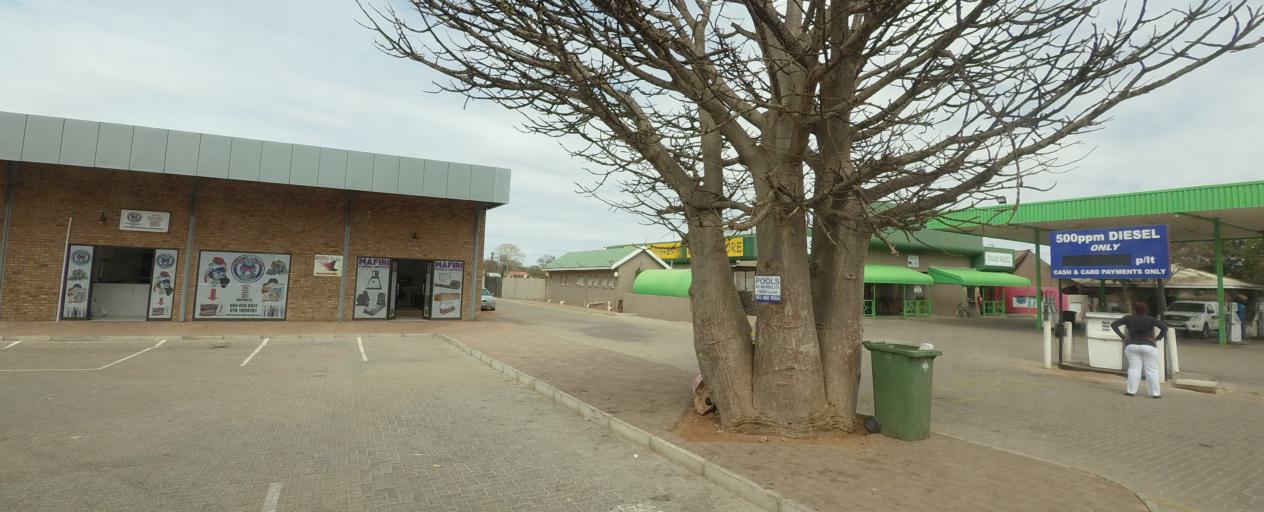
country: BW
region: Central
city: Mathathane
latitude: -22.6800
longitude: 29.1066
